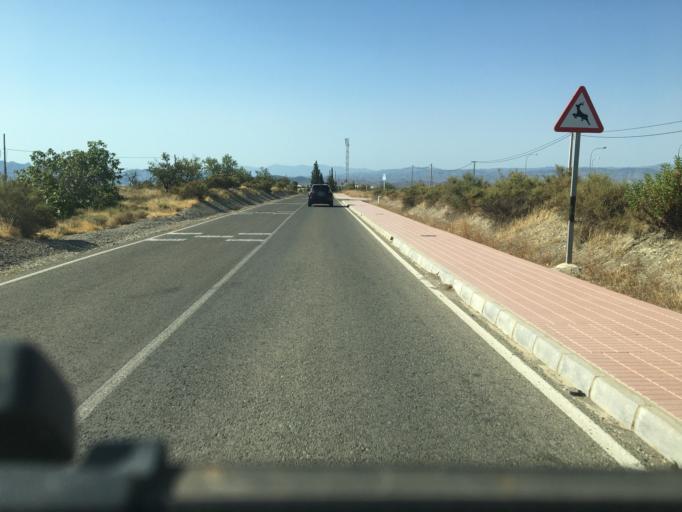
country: ES
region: Andalusia
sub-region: Provincia de Almeria
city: Huercal-Overa
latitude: 37.4554
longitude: -1.9887
